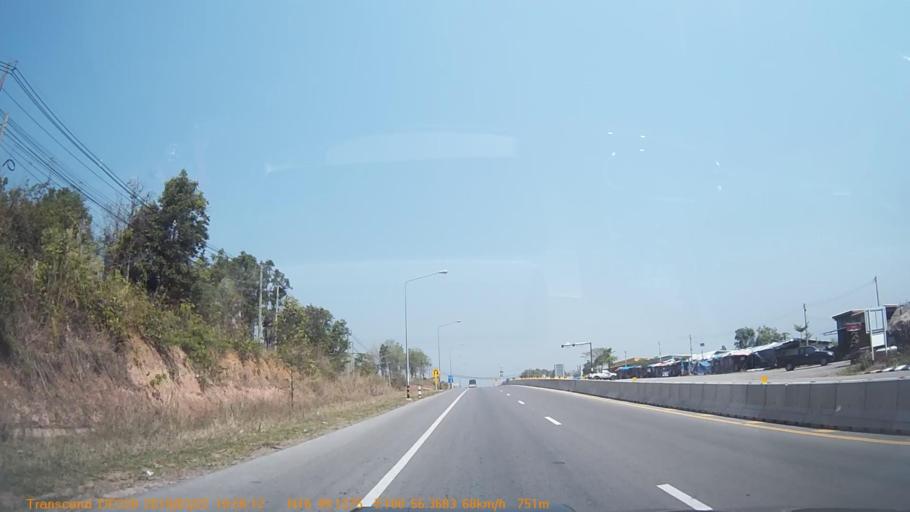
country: TH
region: Phetchabun
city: Khao Kho
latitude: 16.8192
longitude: 100.9394
